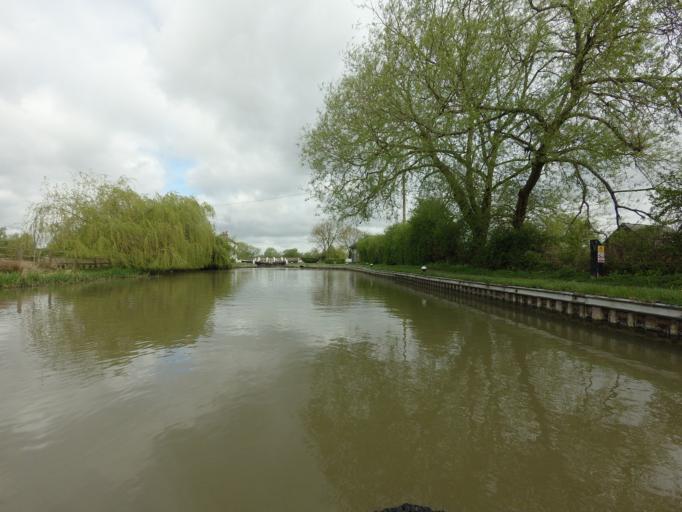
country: GB
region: England
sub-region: Milton Keynes
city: Water Eaton
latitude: 51.9608
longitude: -0.7104
